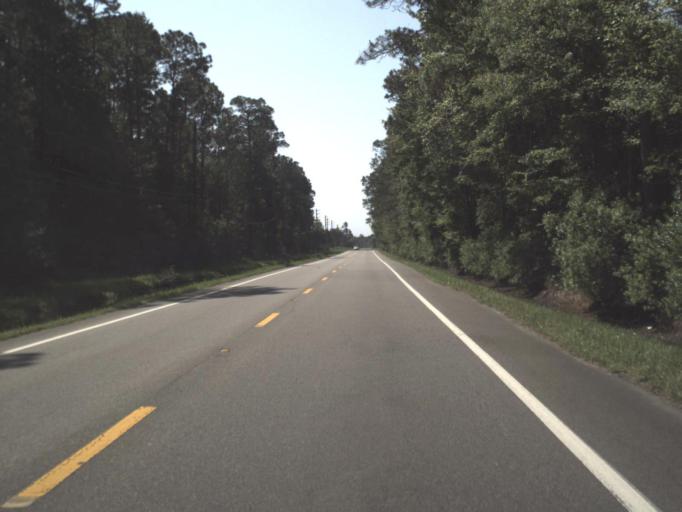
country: US
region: Florida
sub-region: Nassau County
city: Nassau Village-Ratliff
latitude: 30.5004
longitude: -81.7464
